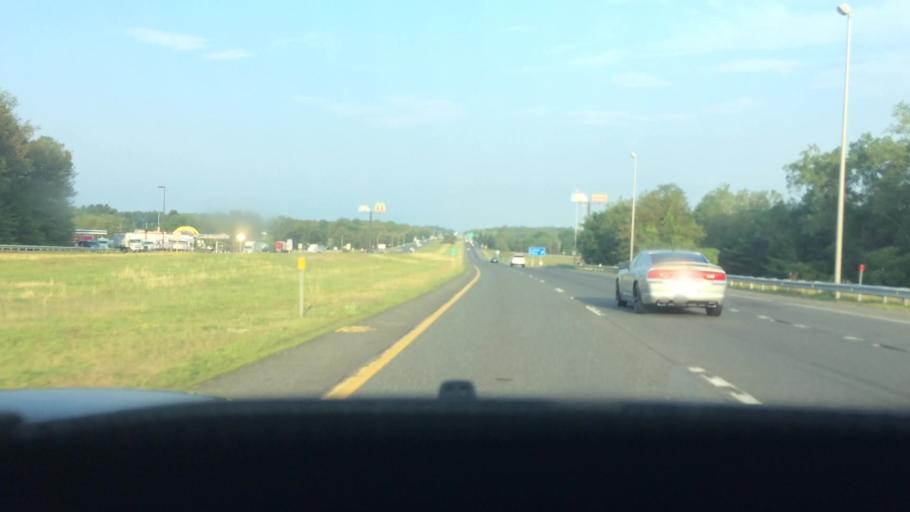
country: US
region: Massachusetts
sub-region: Hampden County
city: Ludlow
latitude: 42.1705
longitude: -72.4504
